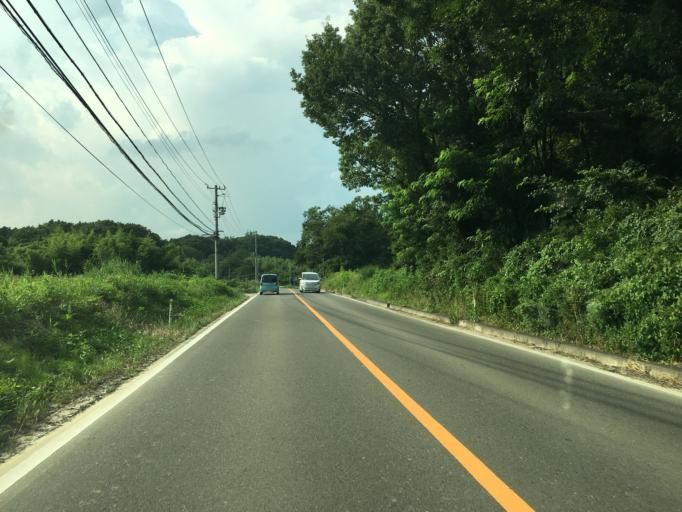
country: JP
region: Fukushima
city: Motomiya
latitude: 37.4661
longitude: 140.4246
